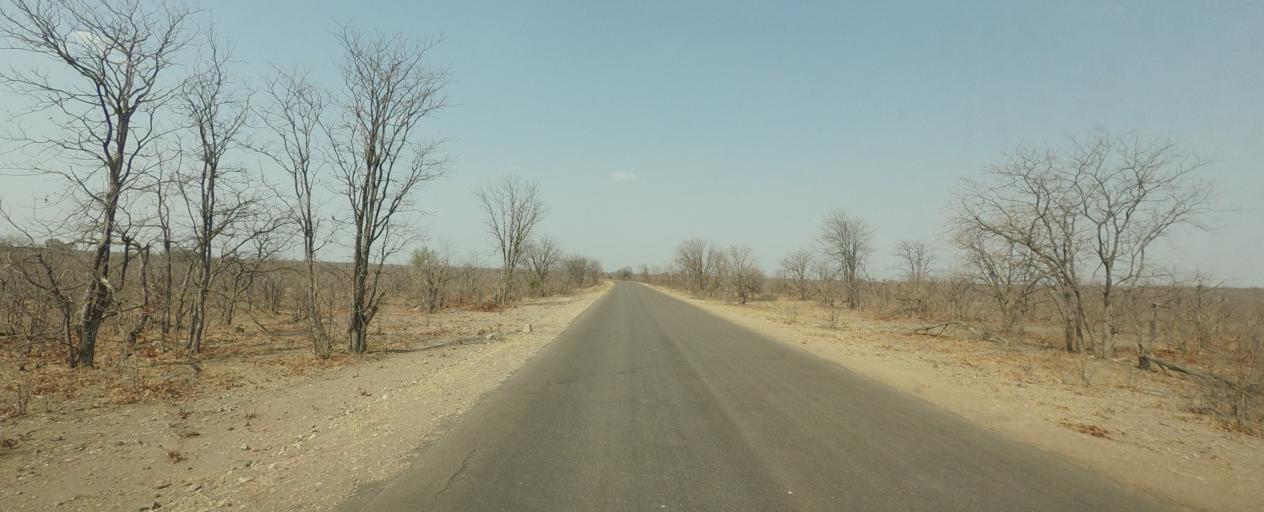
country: ZA
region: Limpopo
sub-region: Mopani District Municipality
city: Giyani
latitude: -23.1673
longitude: 31.3426
